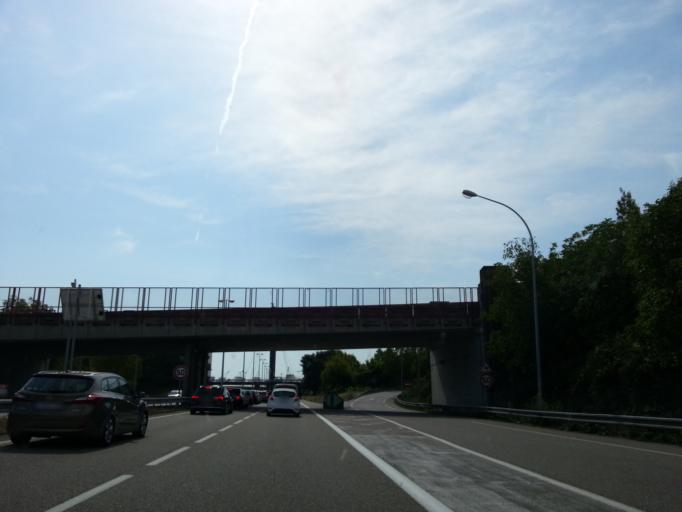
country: FR
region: Alsace
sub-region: Departement du Haut-Rhin
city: Saint-Louis
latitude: 47.5788
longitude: 7.5574
